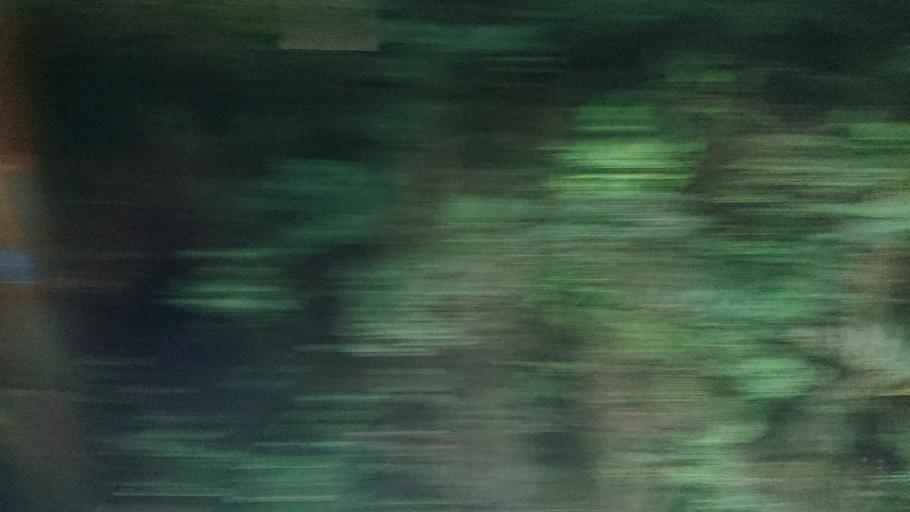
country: TW
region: Taiwan
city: Lugu
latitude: 23.5154
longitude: 120.6985
